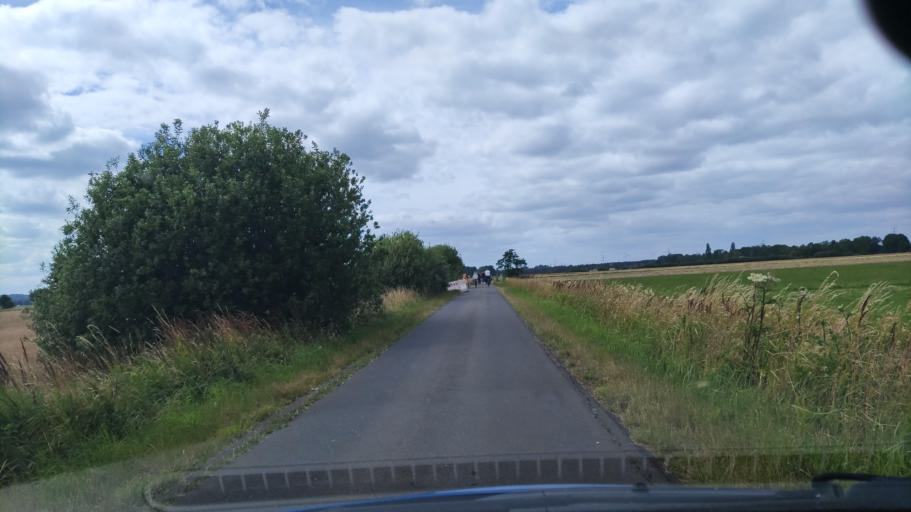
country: DE
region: Lower Saxony
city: Stelle
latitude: 53.4336
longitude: 10.0630
